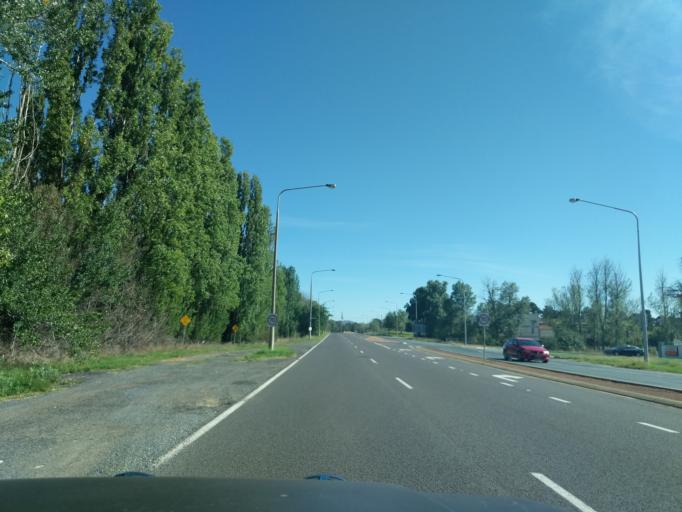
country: AU
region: Australian Capital Territory
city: Forrest
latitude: -35.3422
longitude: 149.1534
